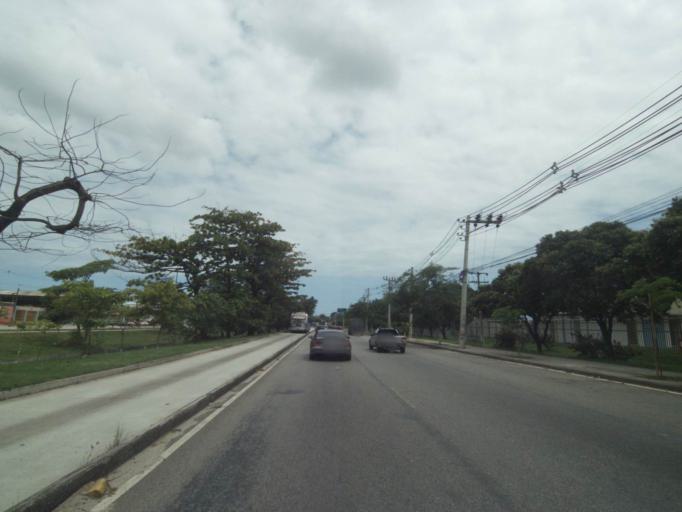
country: BR
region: Rio de Janeiro
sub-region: Sao Joao De Meriti
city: Sao Joao de Meriti
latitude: -22.9419
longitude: -43.3727
